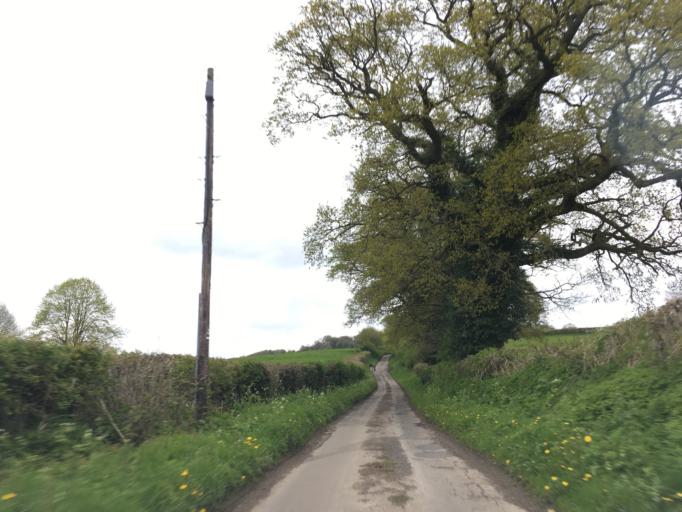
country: GB
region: England
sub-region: Gloucestershire
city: Wotton-under-Edge
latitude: 51.6266
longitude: -2.3500
